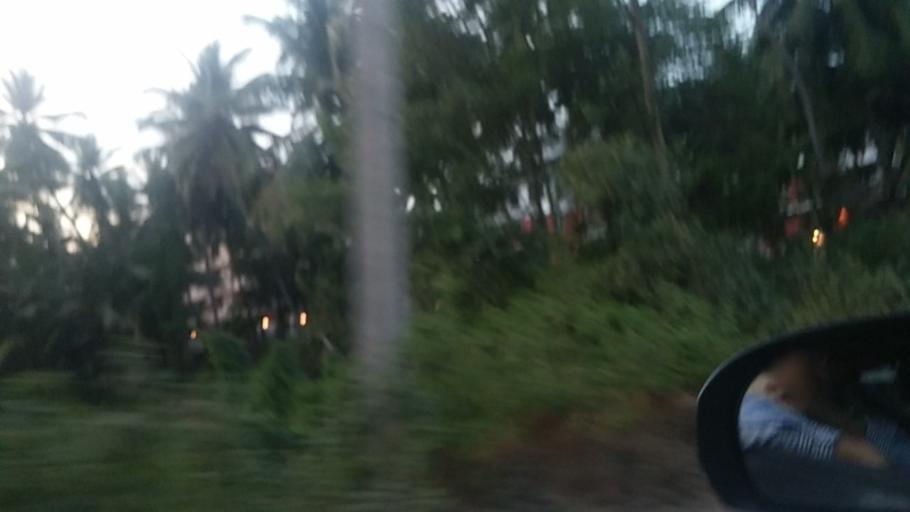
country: IN
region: Goa
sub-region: North Goa
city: Bambolim
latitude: 15.4697
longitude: 73.8464
